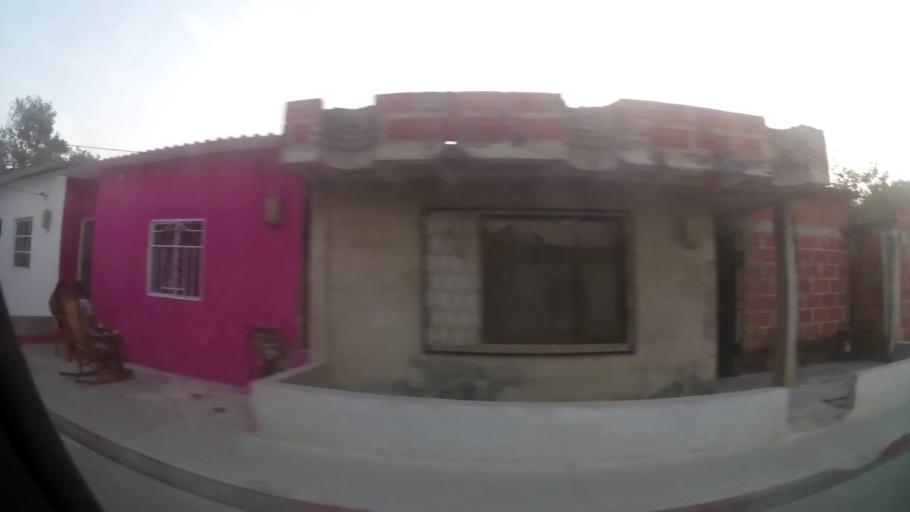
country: CO
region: Atlantico
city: Barranquilla
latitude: 10.9559
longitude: -74.8342
